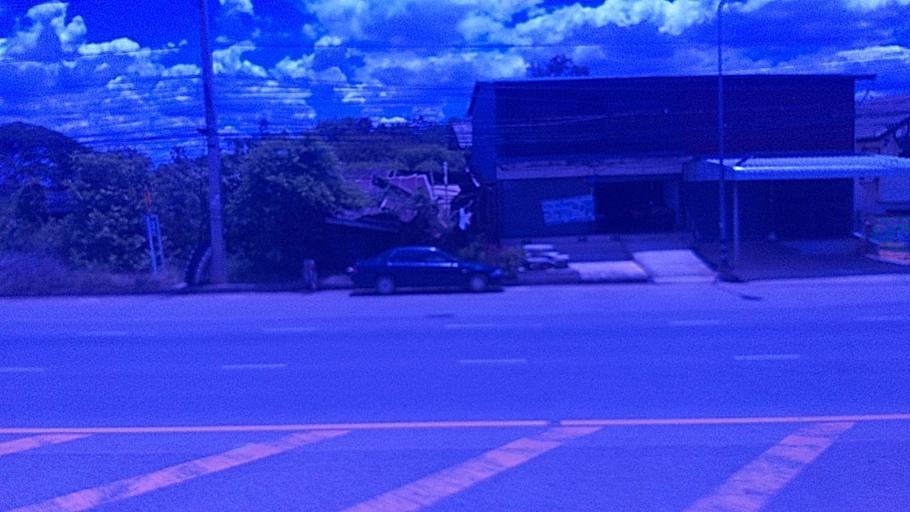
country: TH
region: Chaiyaphum
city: Noen Sa-nga
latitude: 15.6828
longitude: 102.0101
